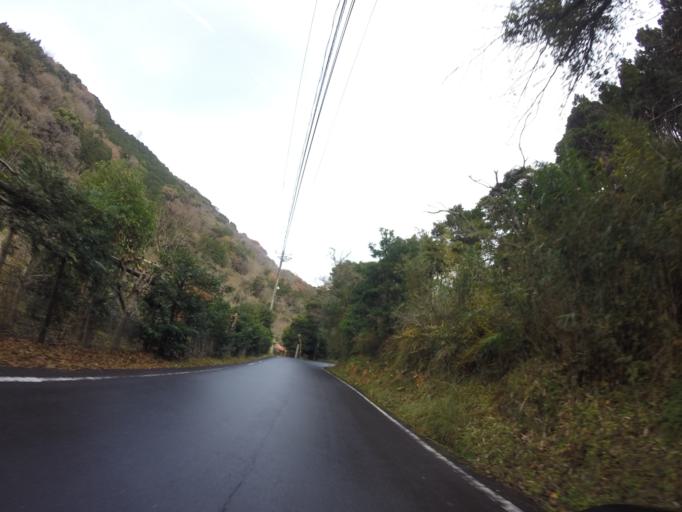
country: JP
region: Shizuoka
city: Heda
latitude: 34.8515
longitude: 138.8014
